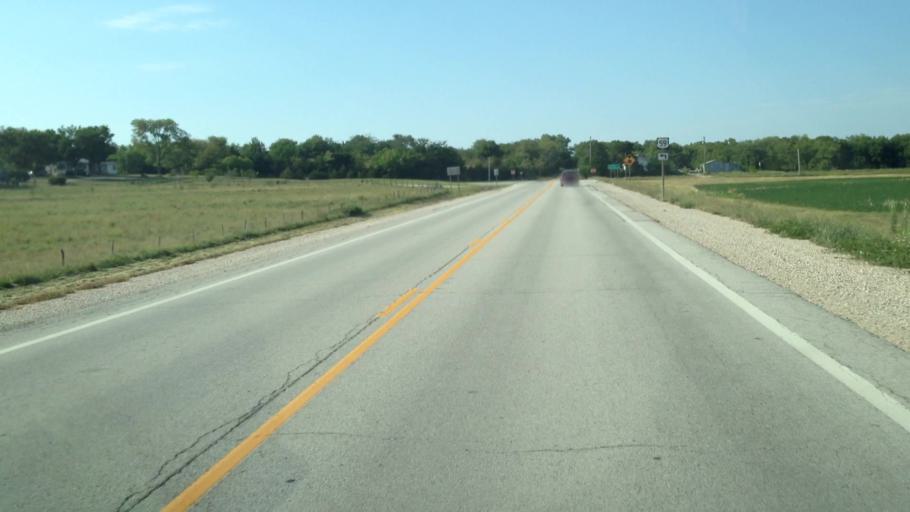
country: US
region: Kansas
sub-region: Anderson County
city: Garnett
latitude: 38.0790
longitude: -95.1694
